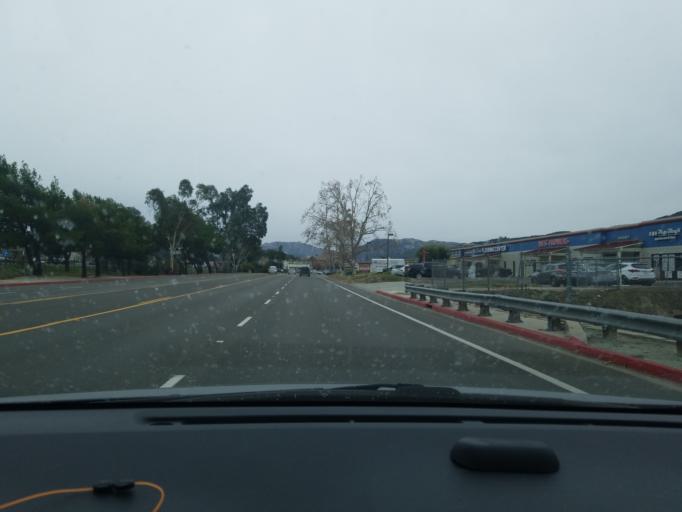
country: US
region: California
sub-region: Riverside County
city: Temecula
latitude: 33.5068
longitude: -117.1550
